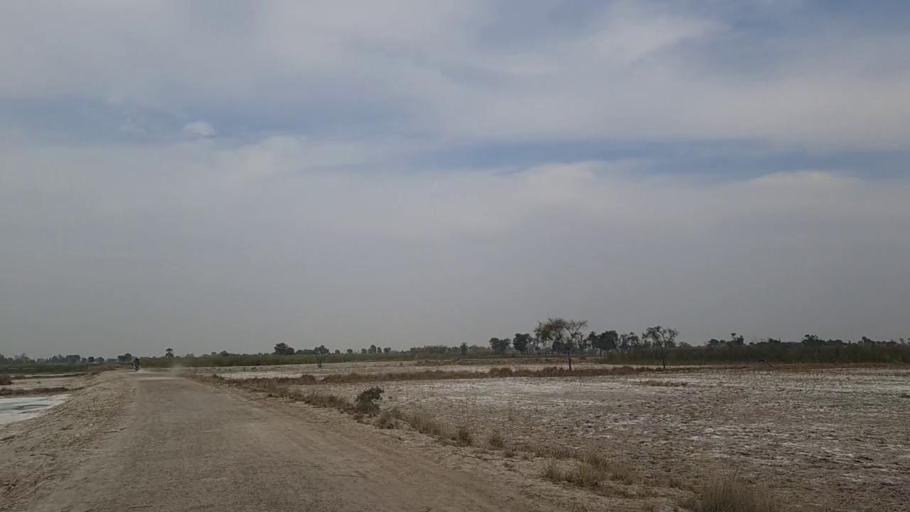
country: PK
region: Sindh
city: Daur
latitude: 26.4975
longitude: 68.3771
